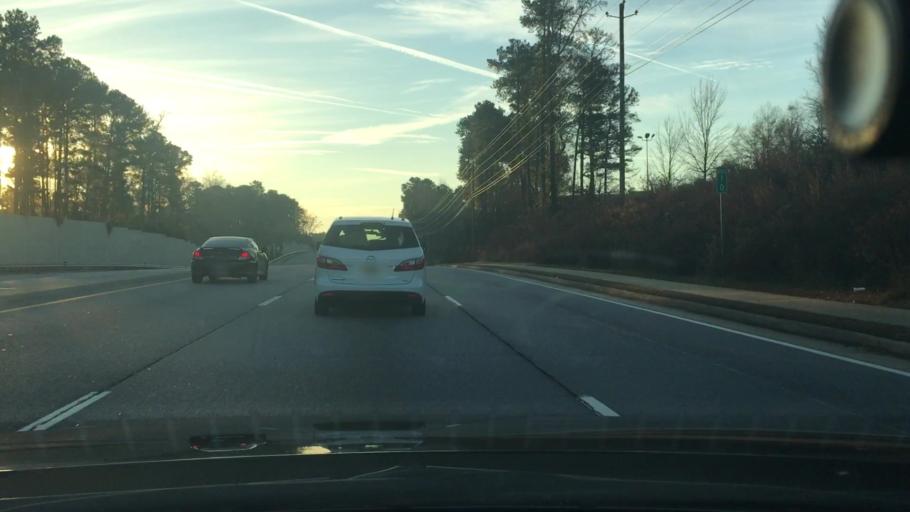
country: US
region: Georgia
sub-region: Fayette County
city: Peachtree City
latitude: 33.3908
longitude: -84.5838
